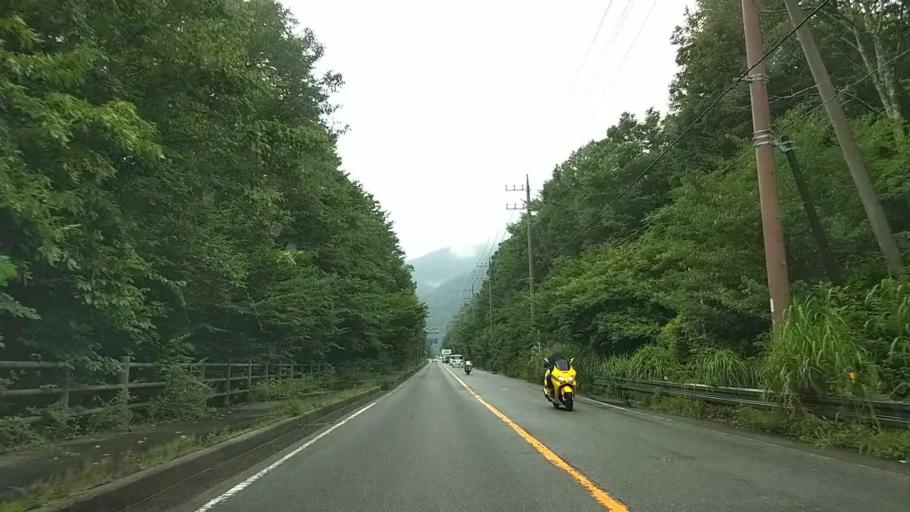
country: JP
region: Yamanashi
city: Fujikawaguchiko
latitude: 35.4859
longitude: 138.6322
